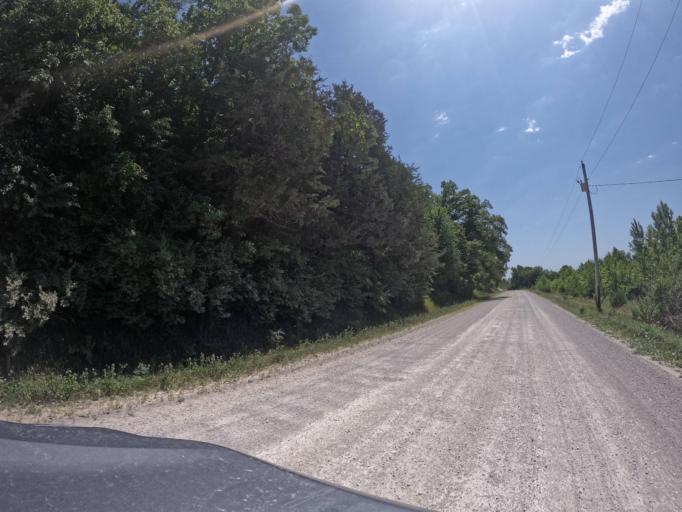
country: US
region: Iowa
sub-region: Henry County
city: Mount Pleasant
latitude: 40.8958
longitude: -91.5491
